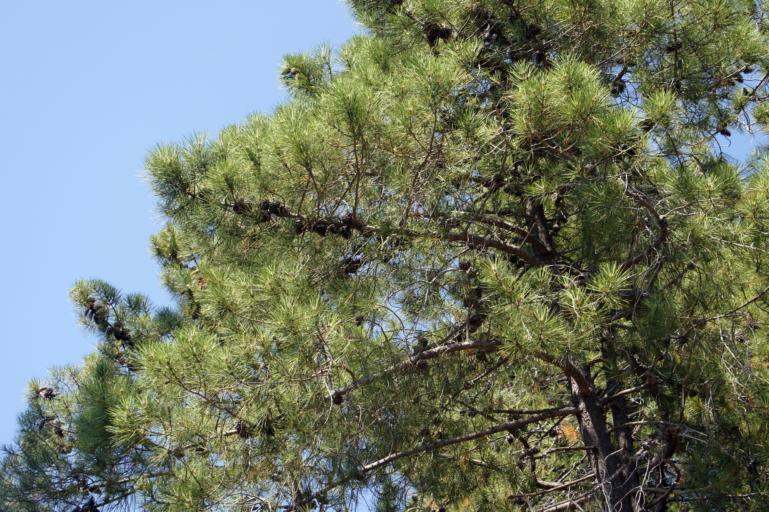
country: FR
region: Corsica
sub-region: Departement de la Corse-du-Sud
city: Cargese
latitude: 42.2498
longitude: 8.6590
